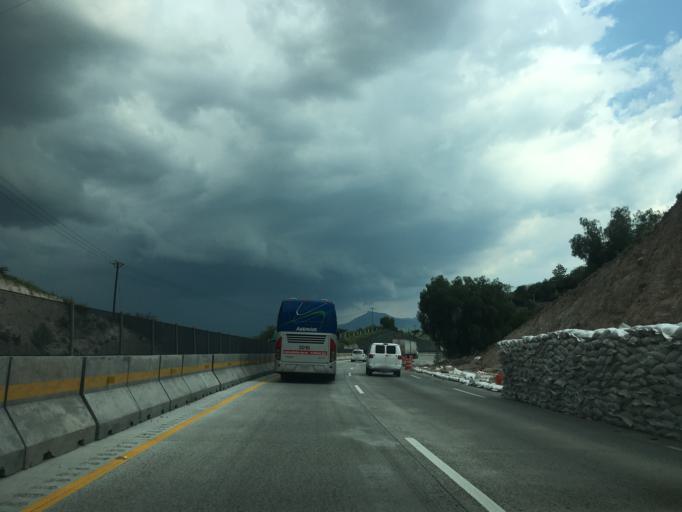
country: MX
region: Hidalgo
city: Tepeji de Ocampo
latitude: 19.9053
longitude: -99.3501
